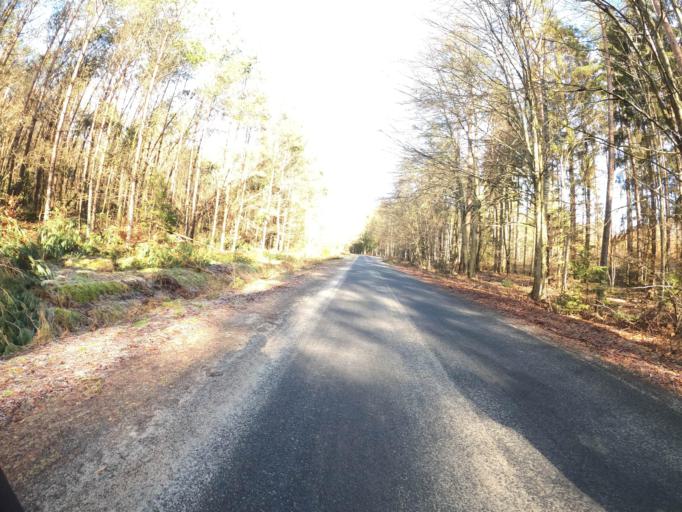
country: PL
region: West Pomeranian Voivodeship
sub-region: Powiat koszalinski
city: Polanow
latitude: 54.1204
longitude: 16.7662
